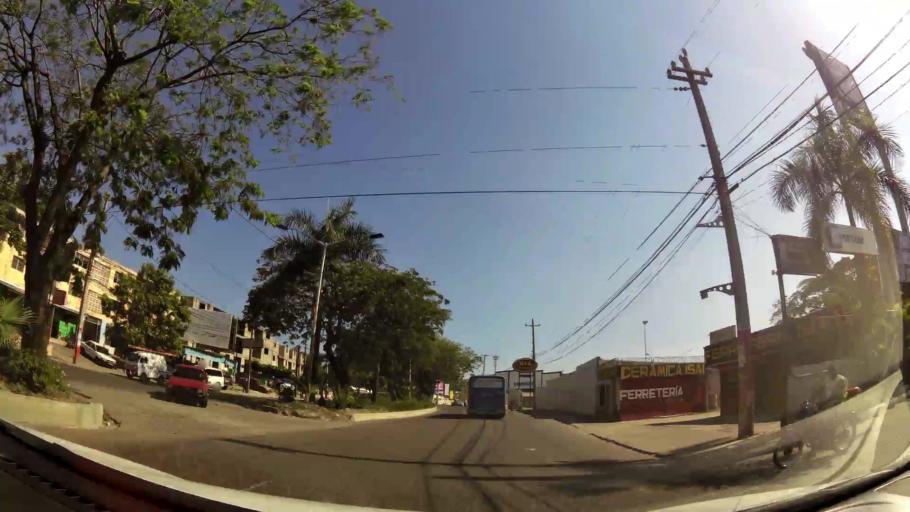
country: DO
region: San Cristobal
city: El Carril
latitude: 18.4625
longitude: -69.9930
